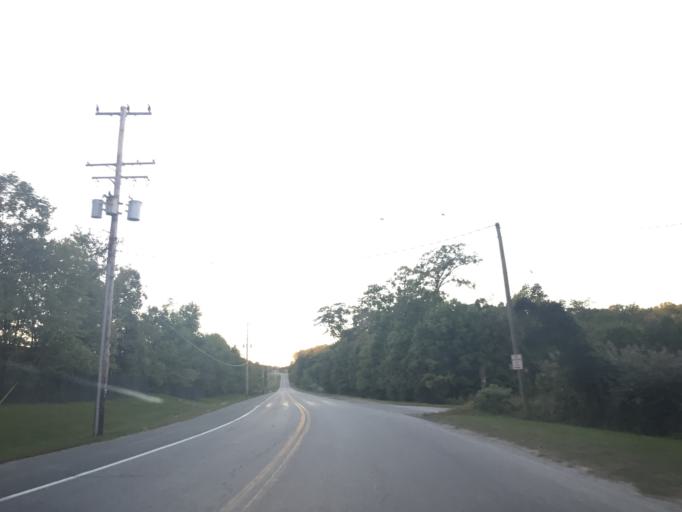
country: US
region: Maryland
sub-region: Baltimore County
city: White Marsh
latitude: 39.3958
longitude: -76.3897
